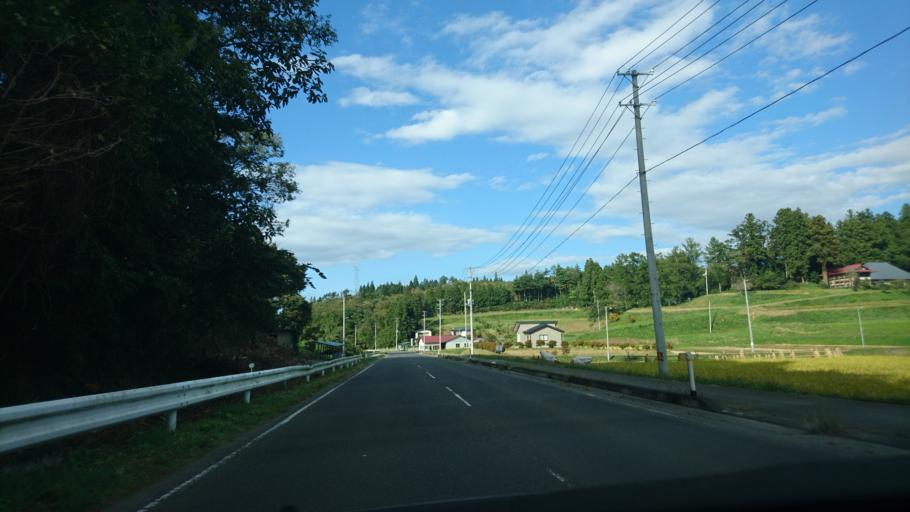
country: JP
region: Iwate
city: Ichinoseki
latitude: 38.8849
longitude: 141.3320
